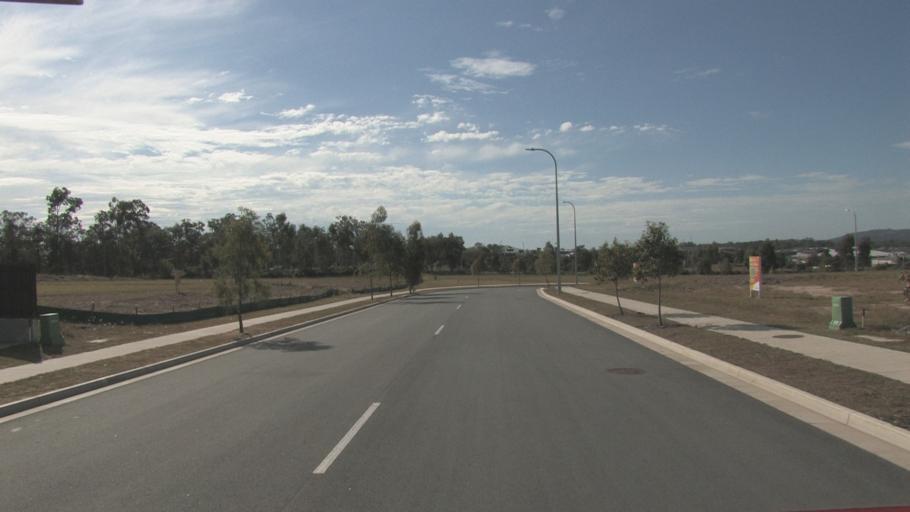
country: AU
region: Queensland
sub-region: Logan
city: Chambers Flat
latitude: -27.8025
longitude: 153.1001
